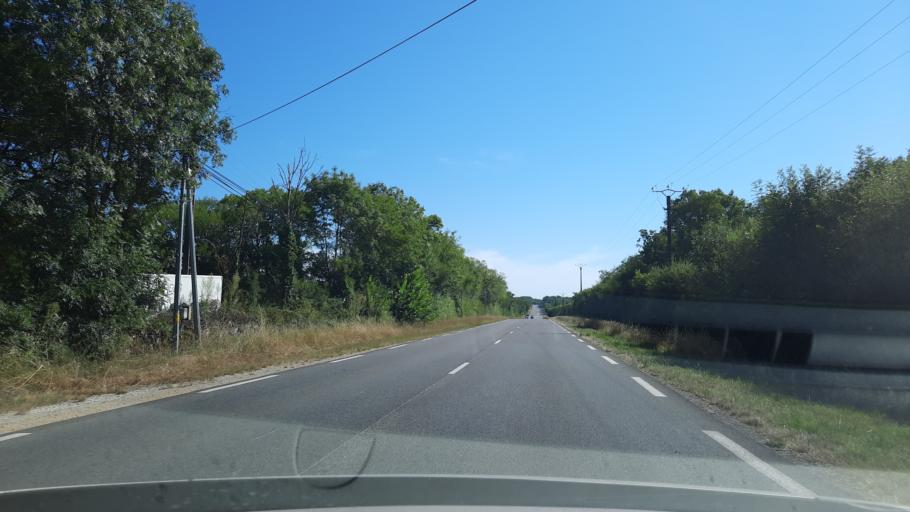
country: FR
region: Midi-Pyrenees
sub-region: Departement du Tarn-et-Garonne
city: Caylus
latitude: 44.2192
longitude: 1.7379
